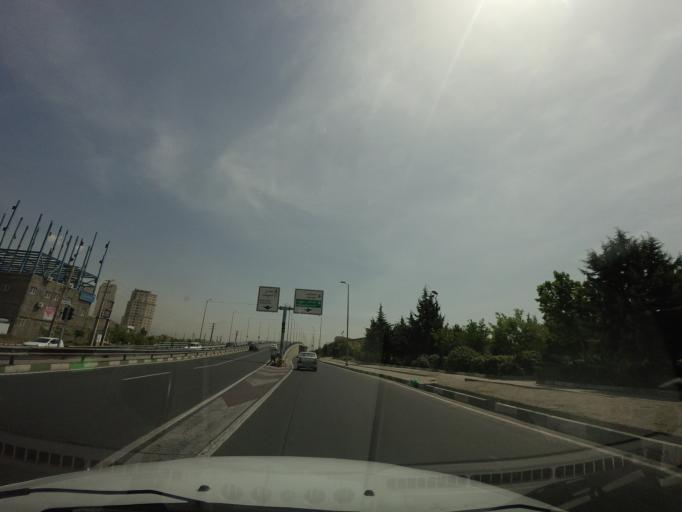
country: IR
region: Tehran
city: Shahr-e Qods
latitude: 35.7459
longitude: 51.2516
